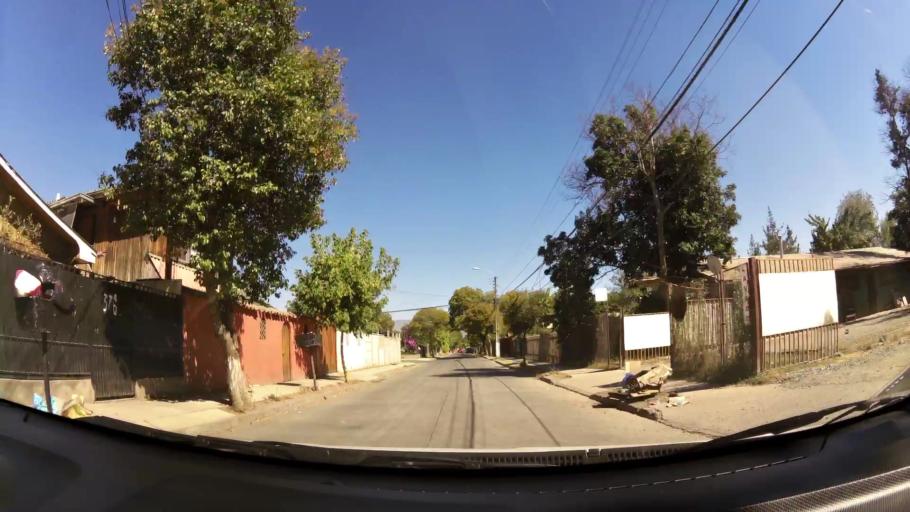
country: CL
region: O'Higgins
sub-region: Provincia de Cachapoal
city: Rancagua
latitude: -34.1700
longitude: -70.7024
